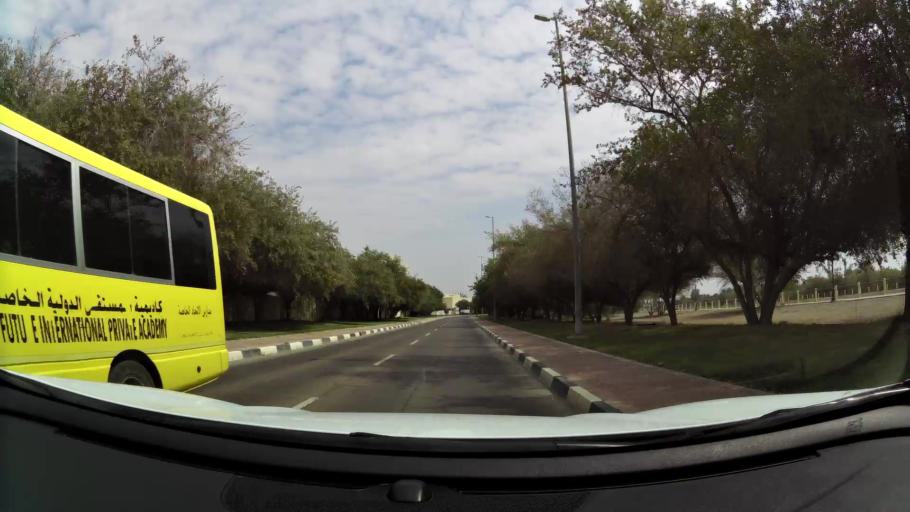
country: OM
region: Al Buraimi
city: Al Buraymi
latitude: 24.2078
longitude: 55.8023
